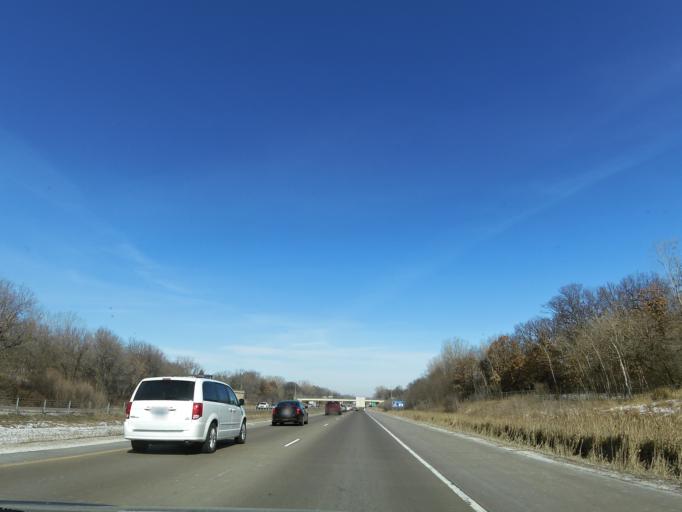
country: US
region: Minnesota
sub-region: Washington County
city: Oakdale
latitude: 44.9835
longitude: -92.9600
